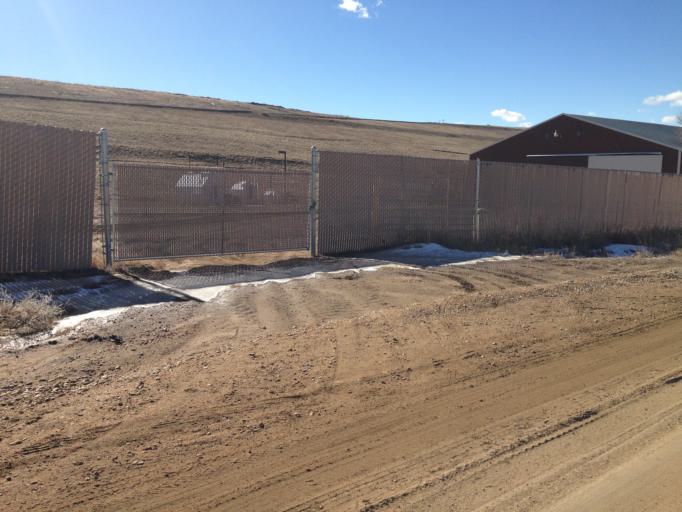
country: US
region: Colorado
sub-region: Boulder County
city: Erie
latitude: 40.0293
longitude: -105.0255
